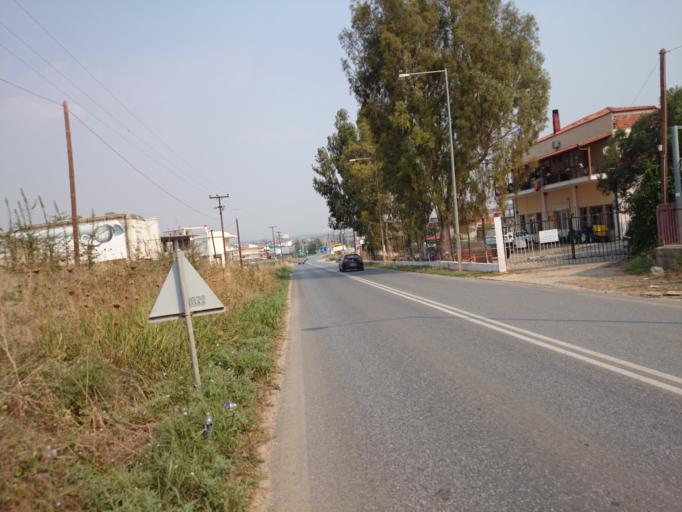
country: GR
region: Central Macedonia
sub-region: Nomos Chalkidikis
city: Nea Moudhania
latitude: 40.2562
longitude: 23.2756
